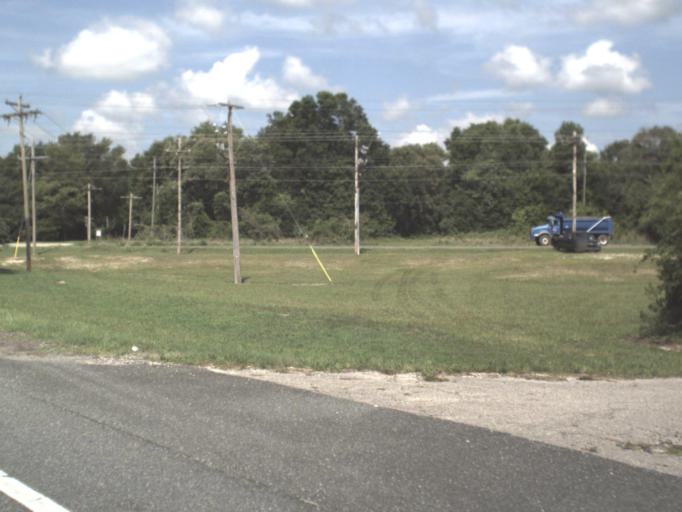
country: US
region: Florida
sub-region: Alachua County
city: Archer
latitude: 29.5686
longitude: -82.4720
